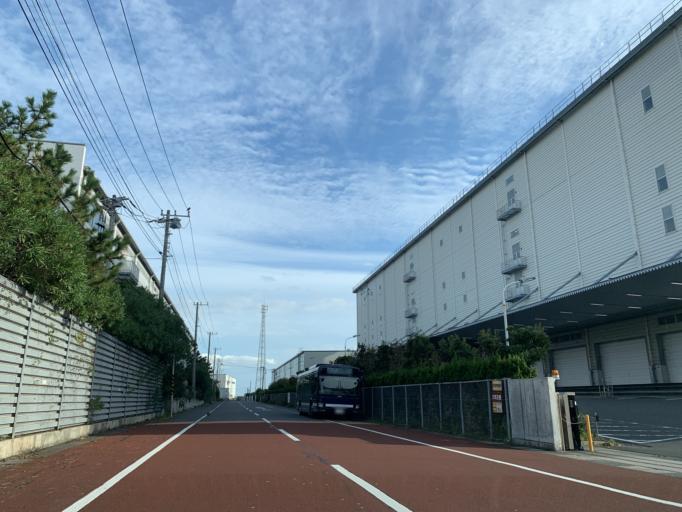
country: JP
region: Tokyo
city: Urayasu
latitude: 35.6273
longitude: 139.9079
